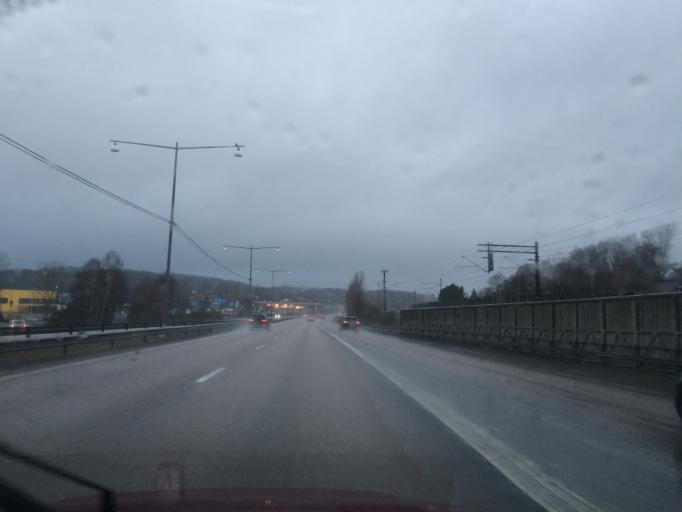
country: SE
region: Vaestra Goetaland
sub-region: Molndal
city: Kallered
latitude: 57.6022
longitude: 12.0543
